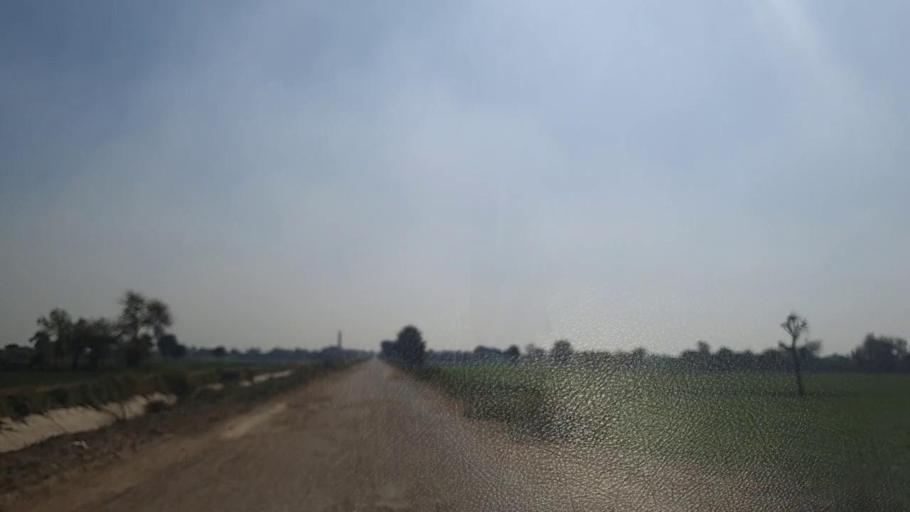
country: PK
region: Sindh
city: Shahpur Chakar
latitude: 26.1945
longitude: 68.5836
